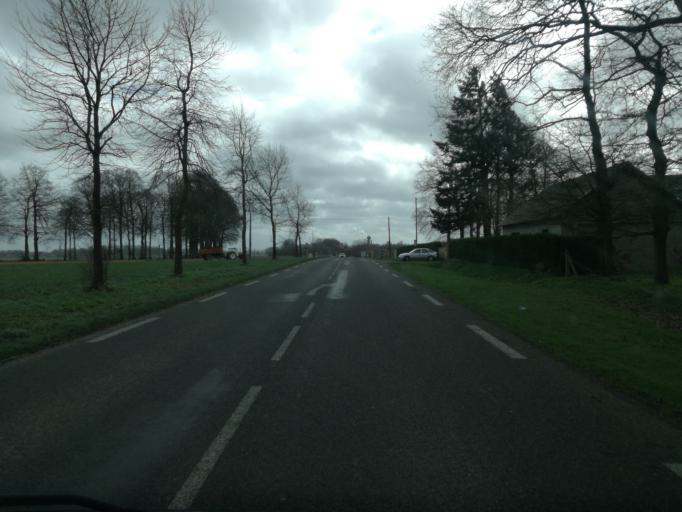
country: FR
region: Haute-Normandie
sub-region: Departement de la Seine-Maritime
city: Valliquerville
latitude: 49.6188
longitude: 0.6565
